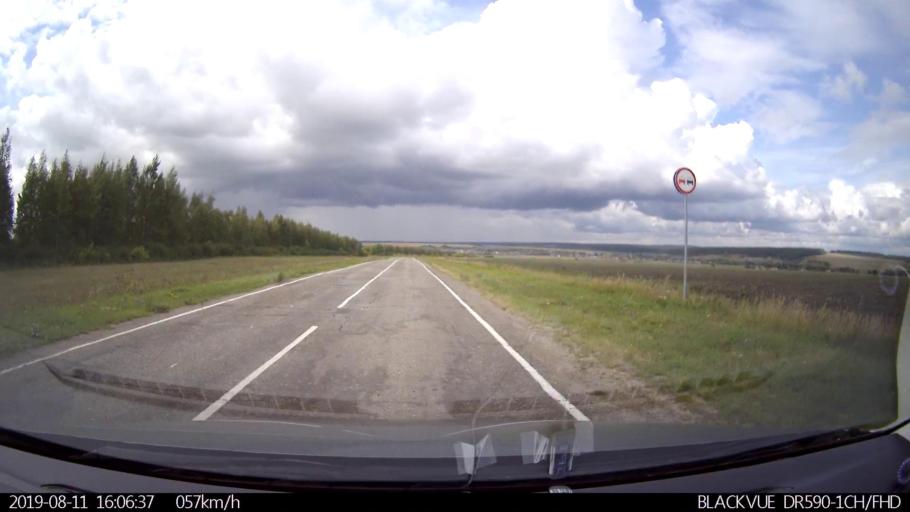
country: RU
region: Ulyanovsk
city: Ignatovka
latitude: 53.9706
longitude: 47.6479
